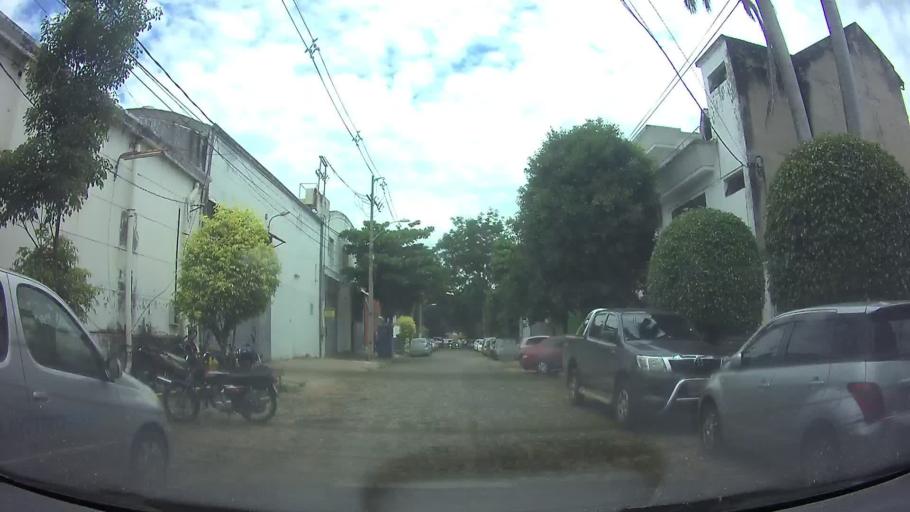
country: PY
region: Central
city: Lambare
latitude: -25.3079
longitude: -57.5854
